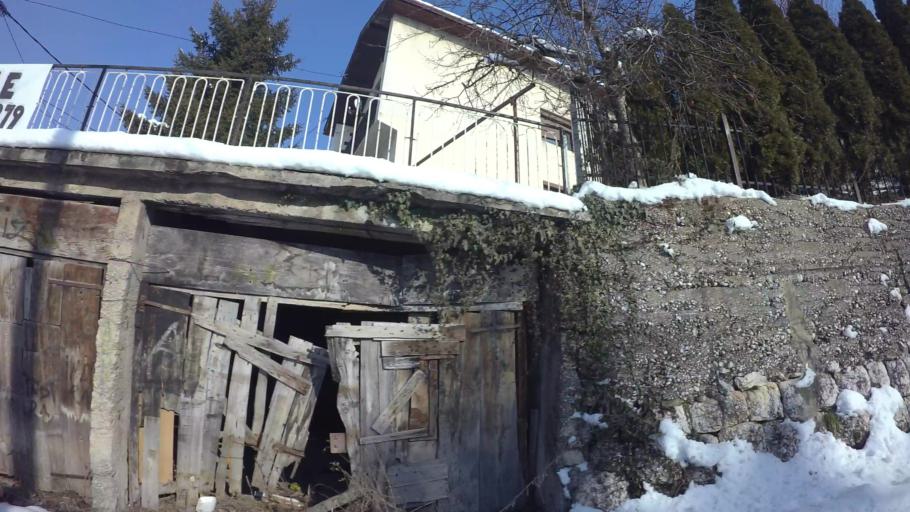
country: BA
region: Federation of Bosnia and Herzegovina
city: Kobilja Glava
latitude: 43.8486
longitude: 18.4057
